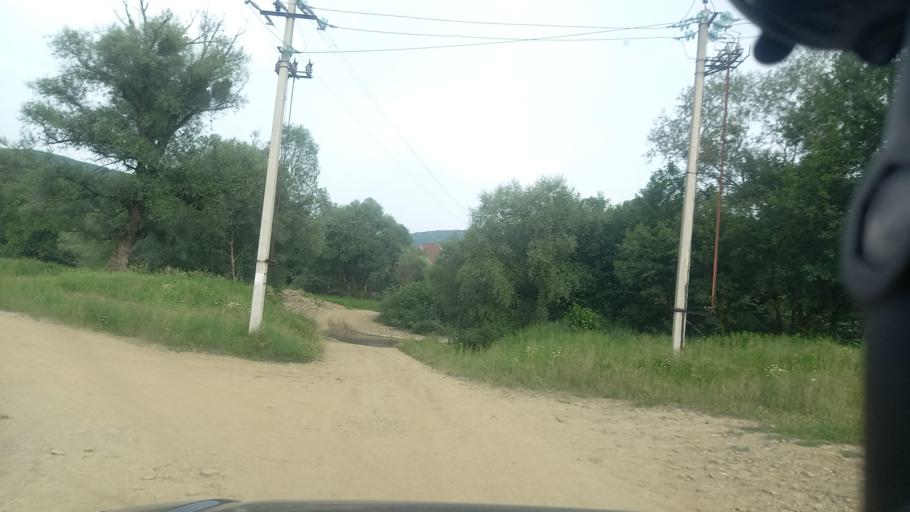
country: RU
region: Krasnodarskiy
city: Goryachiy Klyuch
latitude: 44.6048
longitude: 39.0231
